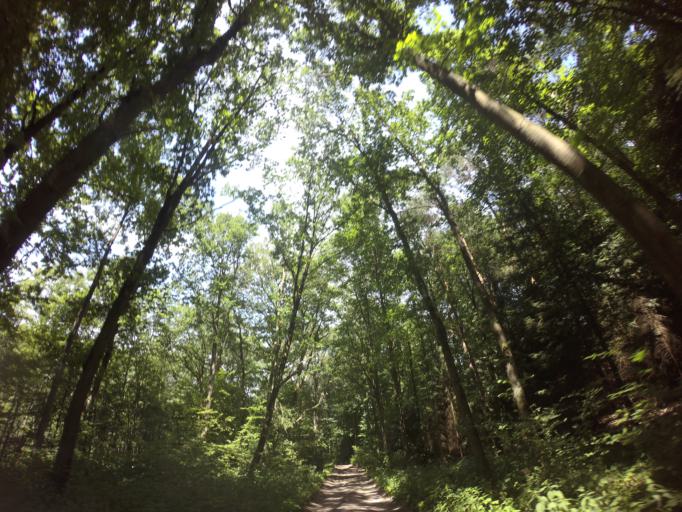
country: PL
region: West Pomeranian Voivodeship
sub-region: Powiat choszczenski
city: Recz
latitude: 53.3255
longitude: 15.5318
